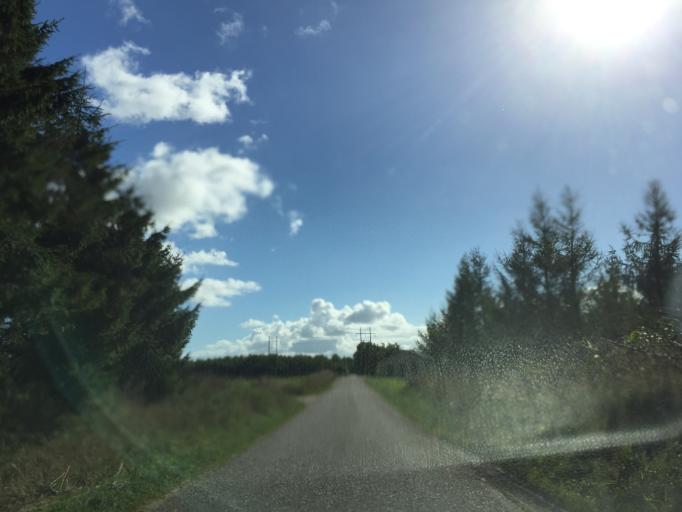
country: DK
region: Central Jutland
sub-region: Viborg Kommune
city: Bjerringbro
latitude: 56.2769
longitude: 9.6854
